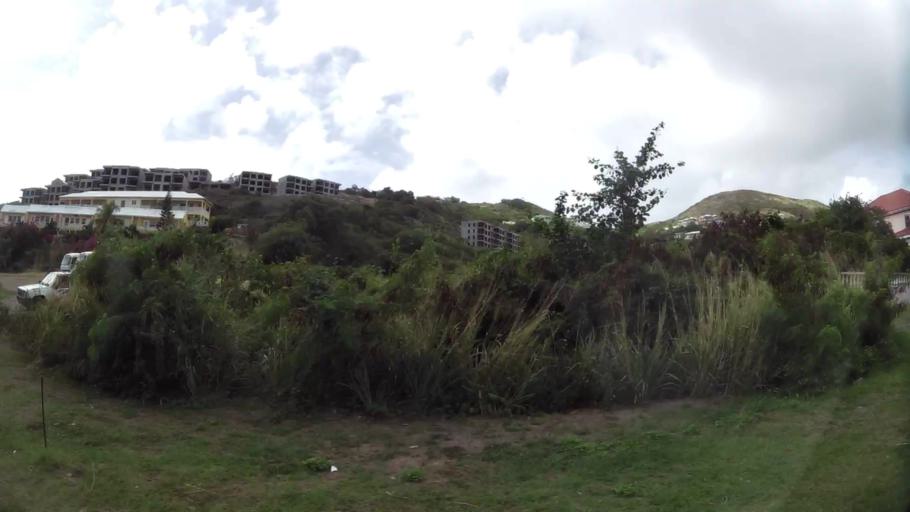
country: KN
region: Saint George Basseterre
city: Basseterre
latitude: 17.2900
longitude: -62.6935
